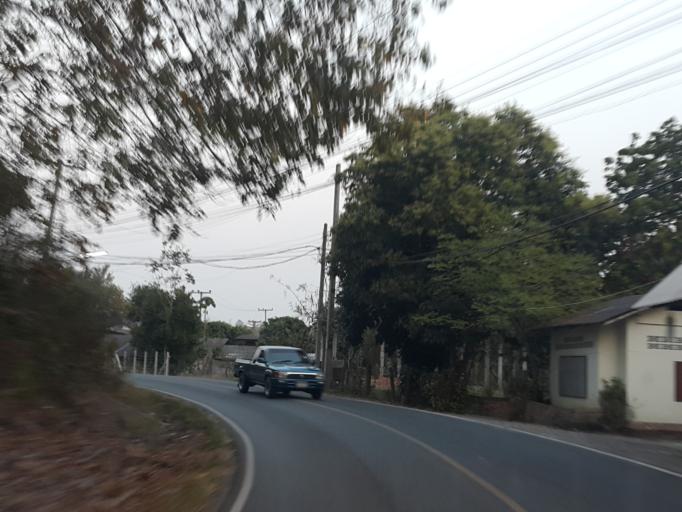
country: TH
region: Chiang Mai
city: Mae Taeng
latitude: 18.9819
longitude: 98.9110
